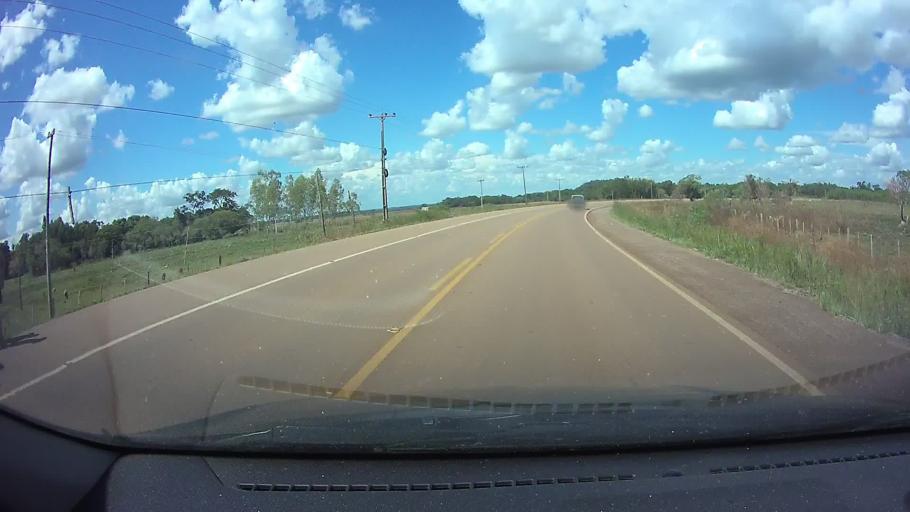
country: PY
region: Paraguari
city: La Colmena
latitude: -25.9145
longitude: -56.7153
